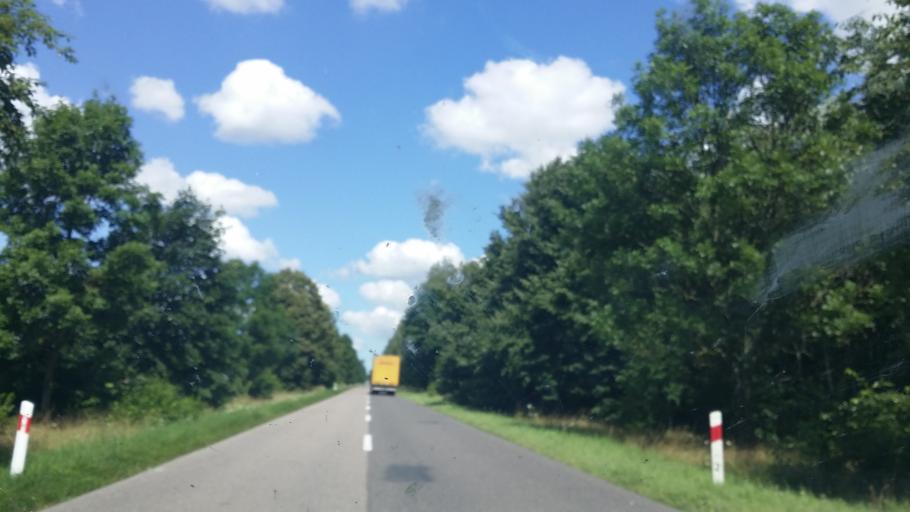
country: PL
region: West Pomeranian Voivodeship
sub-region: Powiat swidwinski
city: Slawoborze
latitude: 53.9291
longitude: 15.6810
